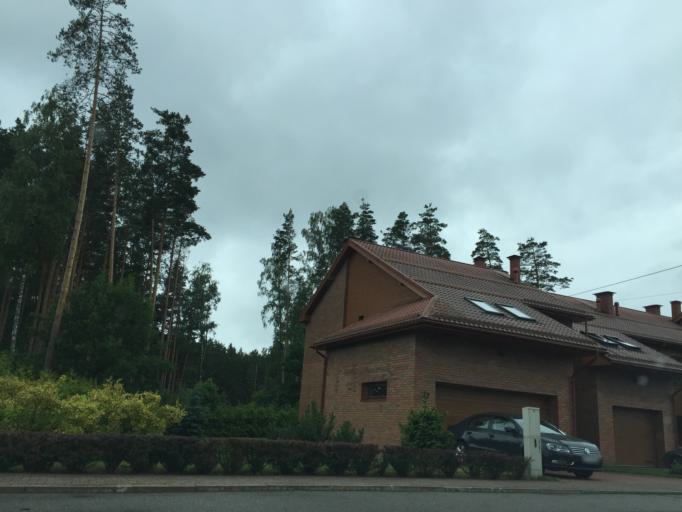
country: LV
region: Riga
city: Jaunciems
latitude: 57.0186
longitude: 24.2176
